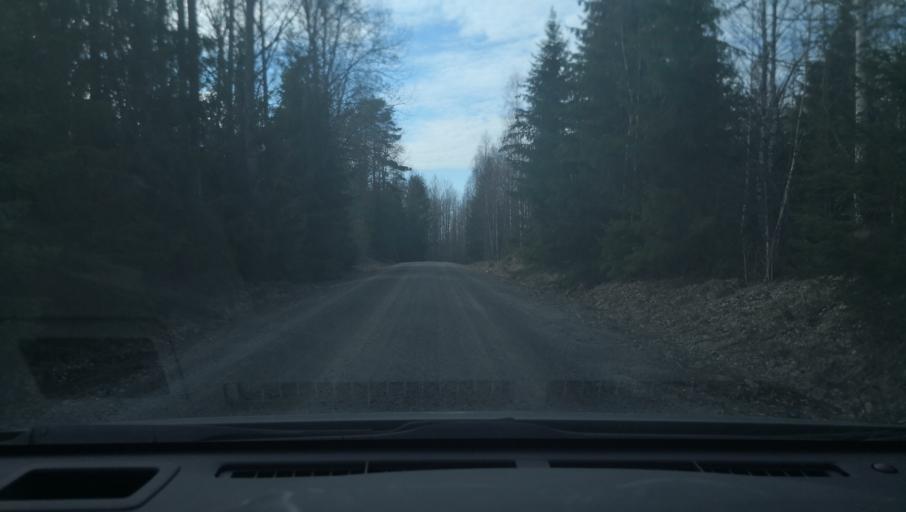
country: SE
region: Uppsala
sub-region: Heby Kommun
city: Heby
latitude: 59.8565
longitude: 16.8582
